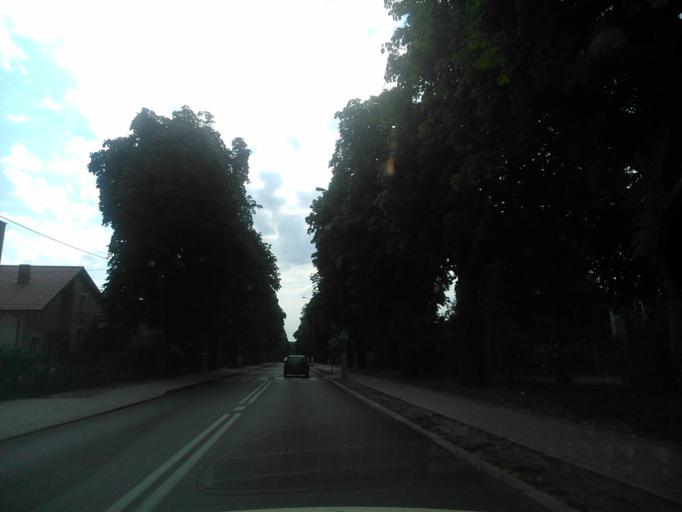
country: PL
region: Warmian-Masurian Voivodeship
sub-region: Powiat dzialdowski
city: Ilowo -Osada
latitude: 53.1715
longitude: 20.2958
